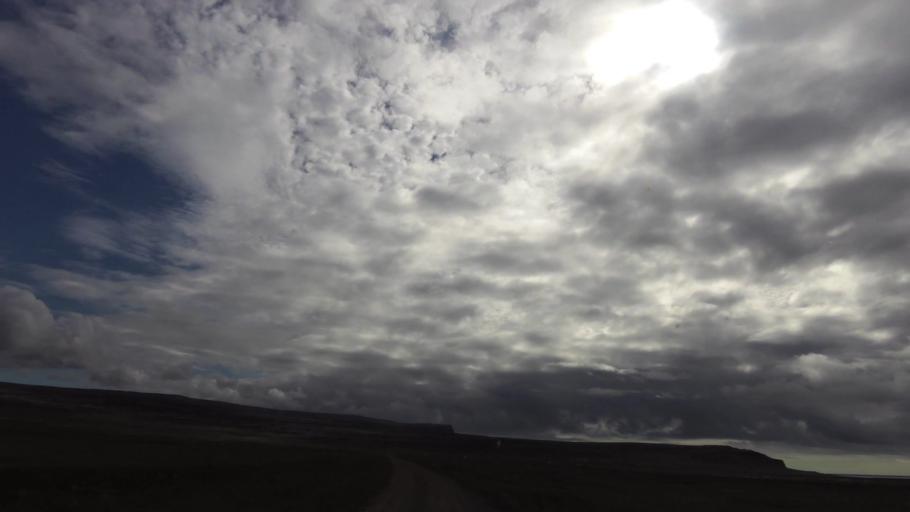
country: IS
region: West
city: Olafsvik
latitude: 65.6138
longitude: -24.3275
